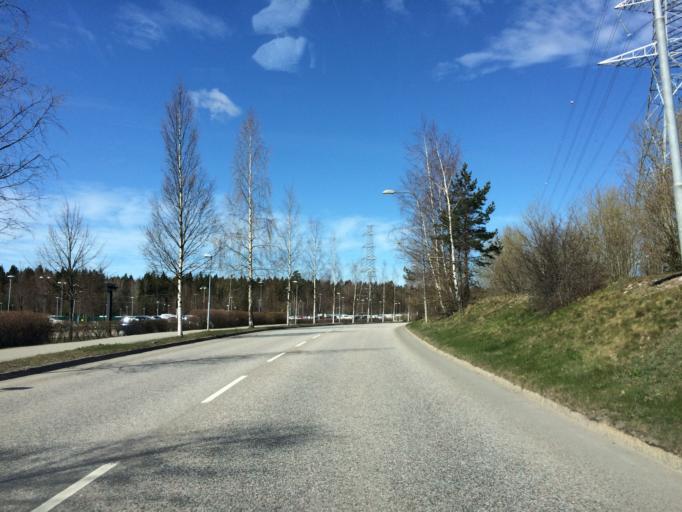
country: SE
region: Stockholm
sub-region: Stockholms Kommun
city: Kista
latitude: 59.4228
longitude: 17.9187
